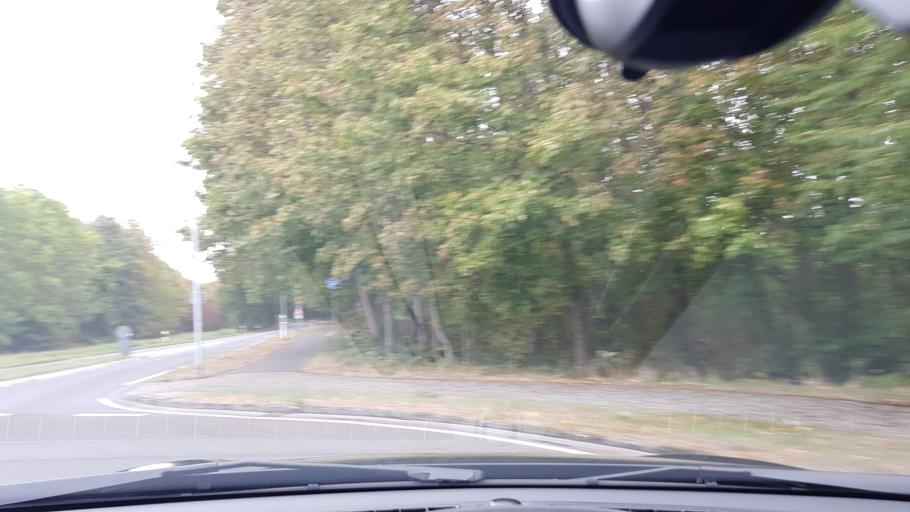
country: DE
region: North Rhine-Westphalia
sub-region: Regierungsbezirk Koln
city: Elsdorf
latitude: 50.9430
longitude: 6.5665
